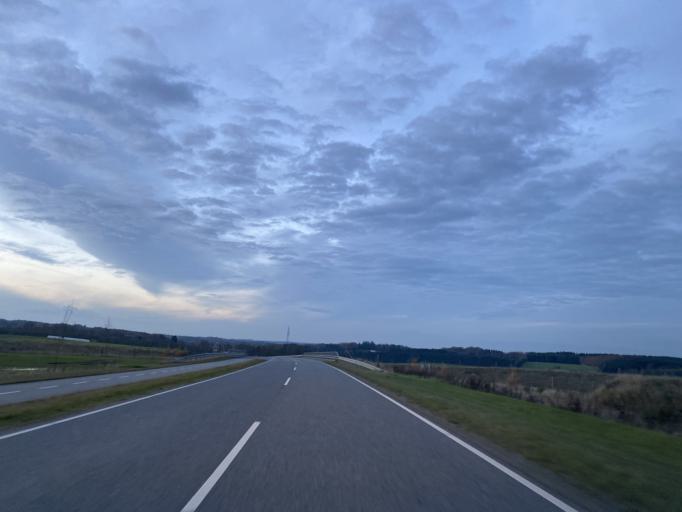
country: DK
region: Central Jutland
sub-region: Silkeborg Kommune
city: Svejbaek
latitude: 56.1464
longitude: 9.7049
